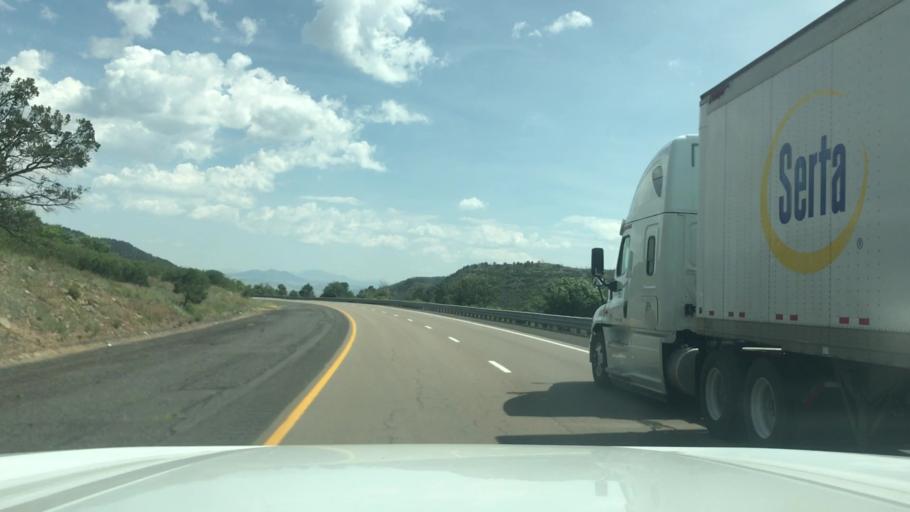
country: US
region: New Mexico
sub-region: Colfax County
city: Raton
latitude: 36.9365
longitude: -104.4659
